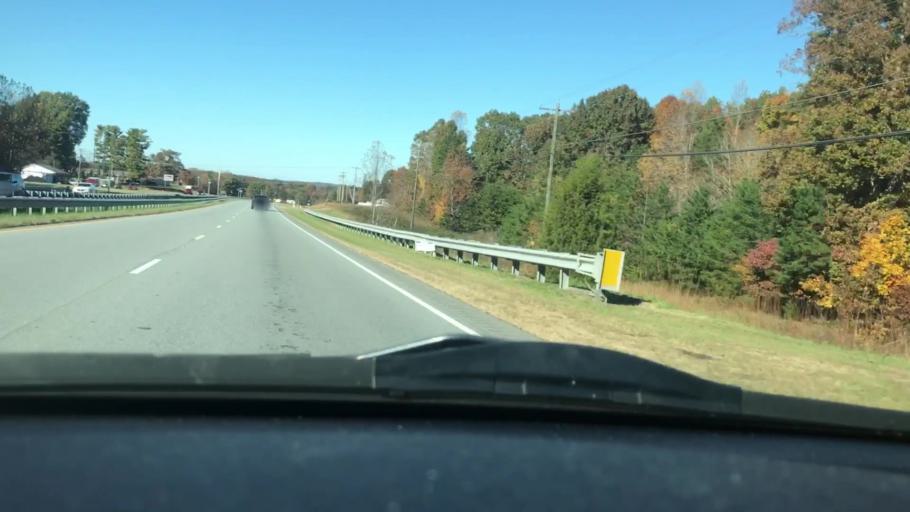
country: US
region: North Carolina
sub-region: Rockingham County
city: Madison
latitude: 36.3497
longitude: -79.9458
